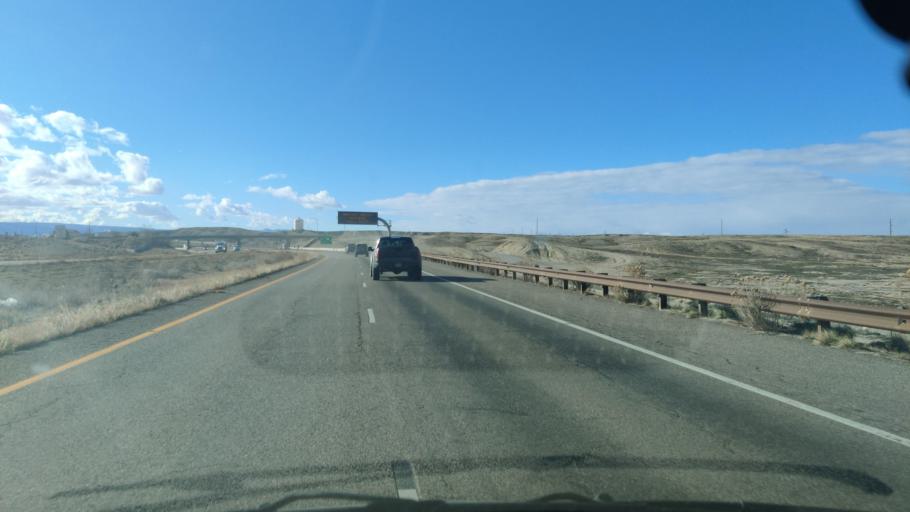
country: US
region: Colorado
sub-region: Mesa County
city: Clifton
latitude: 39.1078
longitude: -108.4367
